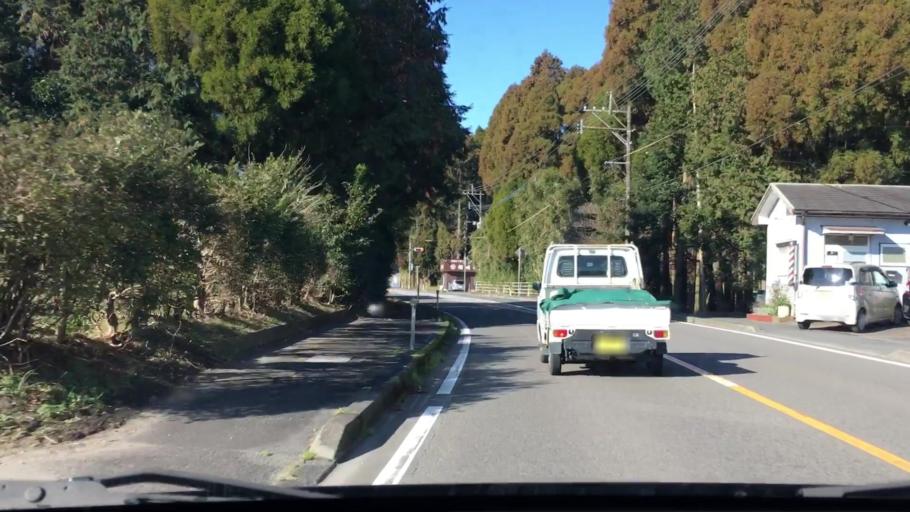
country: JP
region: Kagoshima
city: Kokubu-matsuki
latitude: 31.6725
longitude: 130.8594
